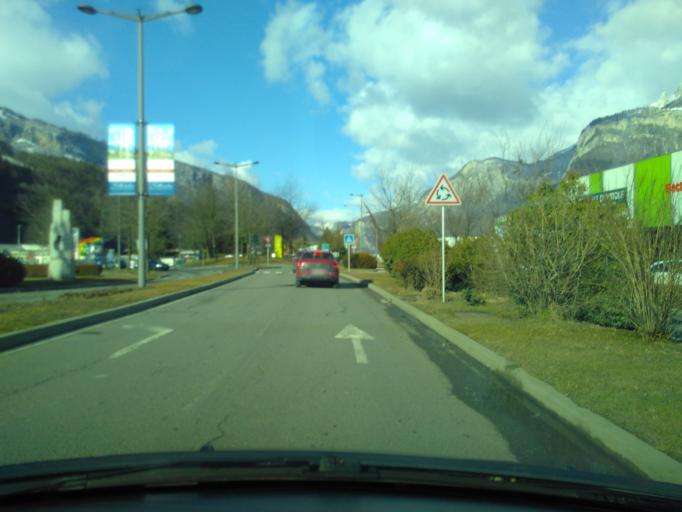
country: FR
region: Rhone-Alpes
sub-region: Departement de la Haute-Savoie
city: Sallanches
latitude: 45.9513
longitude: 6.6300
